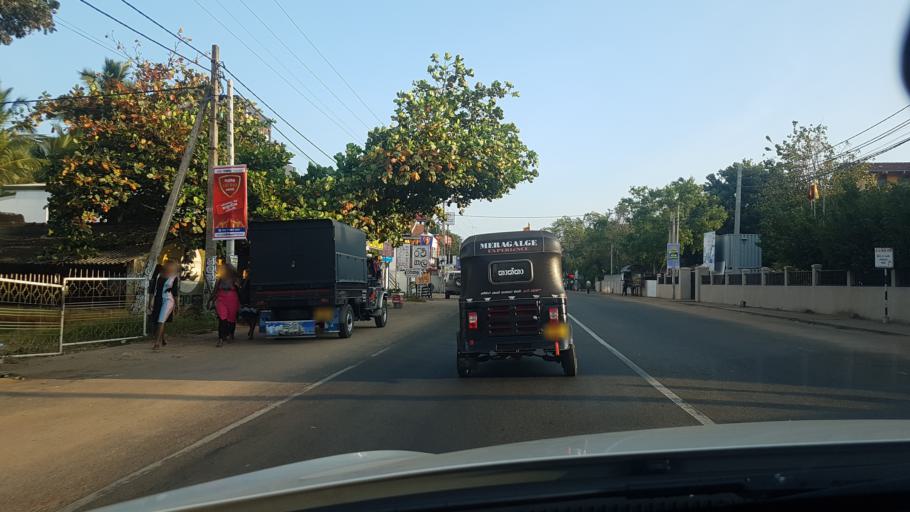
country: LK
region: North Western
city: Chilaw
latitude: 7.5724
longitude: 79.7974
